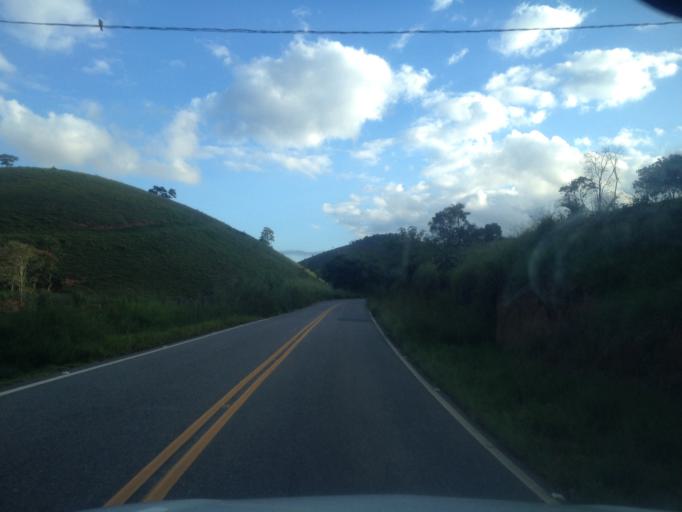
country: BR
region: Rio de Janeiro
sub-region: Quatis
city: Quatis
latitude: -22.3669
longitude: -44.2577
